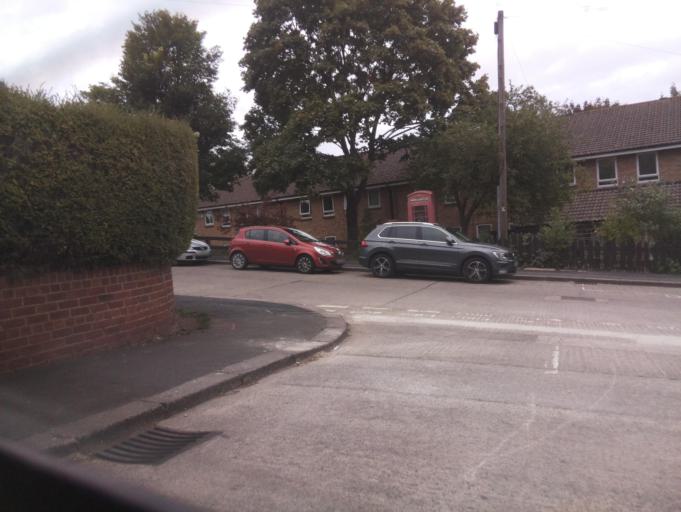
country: GB
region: England
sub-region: North Somerset
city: Easton-in-Gordano
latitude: 51.4945
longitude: -2.6483
